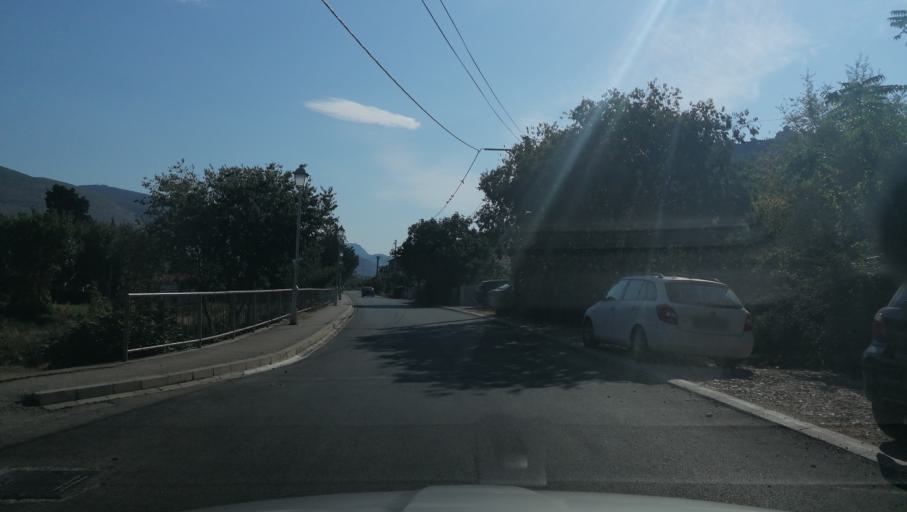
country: BA
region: Republika Srpska
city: Trebinje
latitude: 42.7136
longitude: 18.3536
